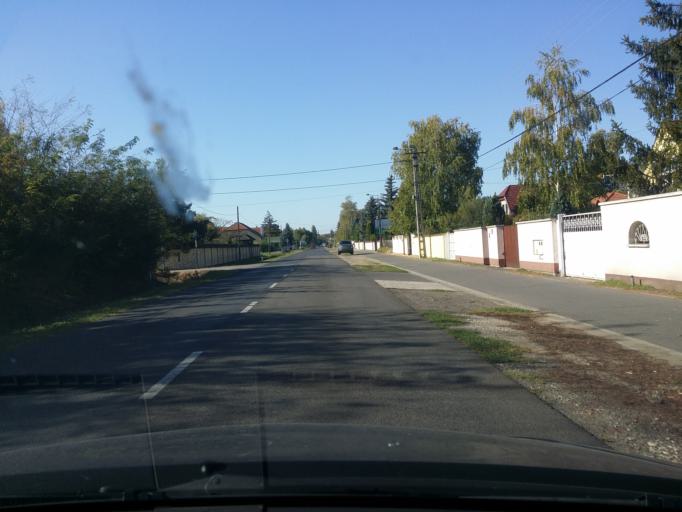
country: HU
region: Bekes
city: Bekescsaba
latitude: 46.6883
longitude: 21.1188
